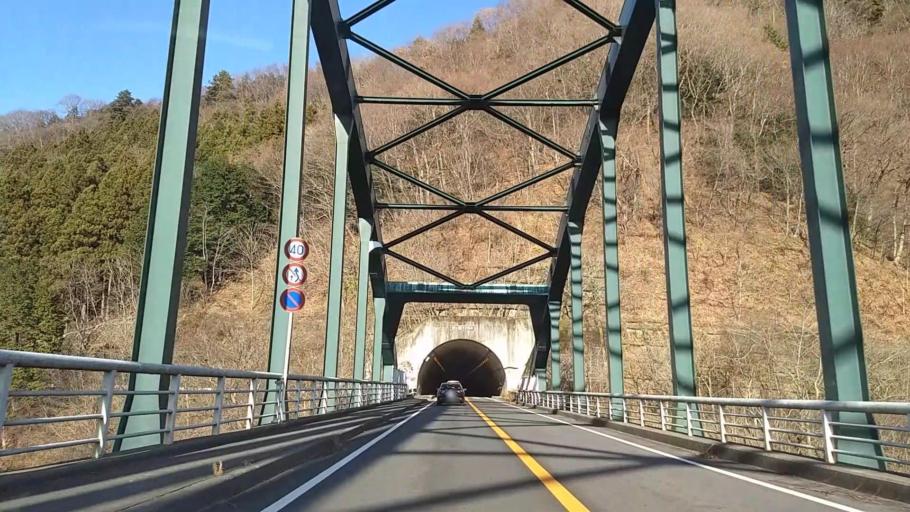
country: JP
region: Yamanashi
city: Uenohara
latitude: 35.5273
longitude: 139.2358
